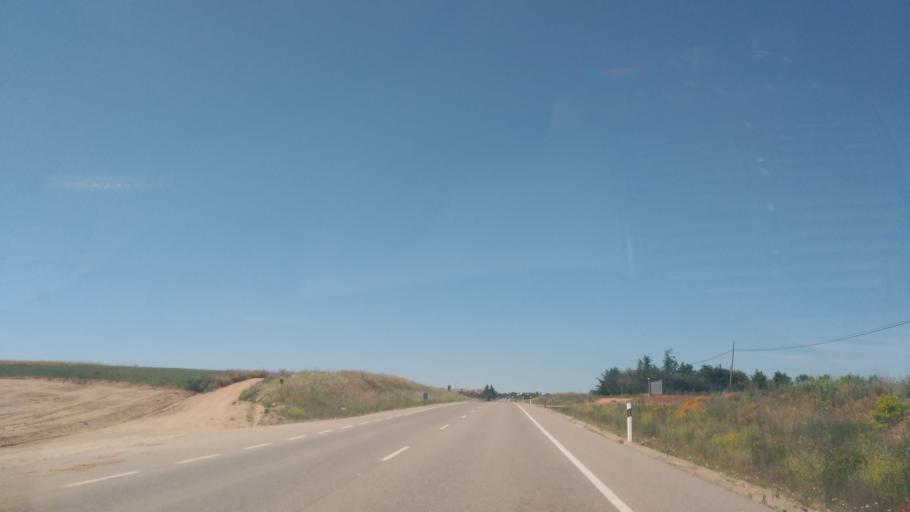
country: ES
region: Castille and Leon
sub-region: Provincia de Salamanca
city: Villares de la Reina
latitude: 41.0077
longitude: -5.6683
